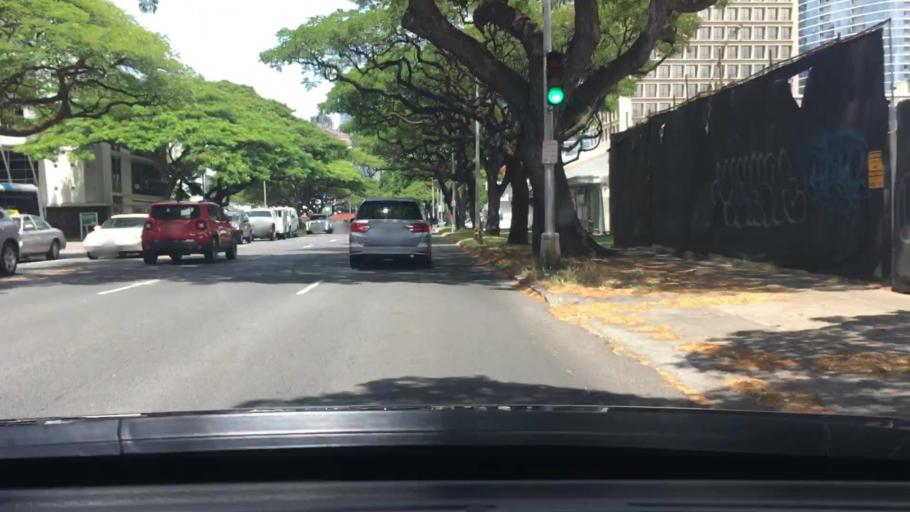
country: US
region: Hawaii
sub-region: Honolulu County
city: Honolulu
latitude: 21.2940
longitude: -157.8443
